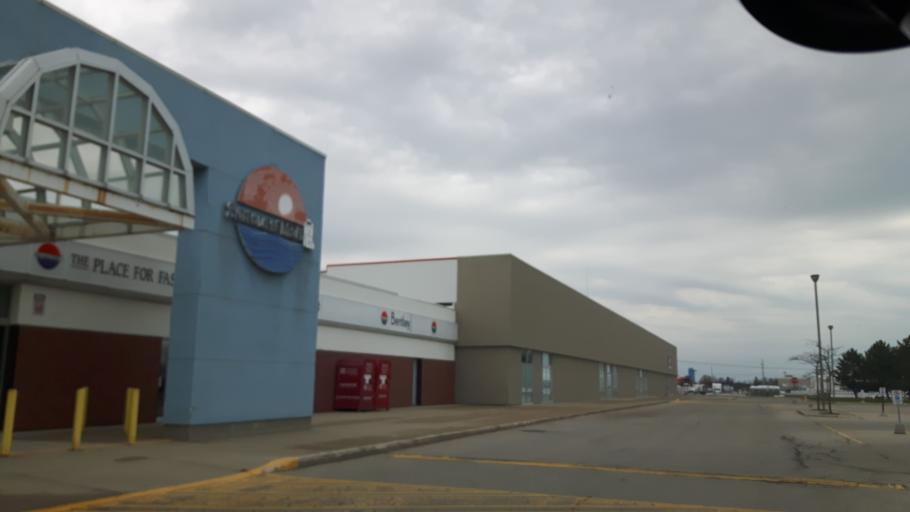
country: CA
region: Ontario
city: Goderich
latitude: 43.7294
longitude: -81.7043
